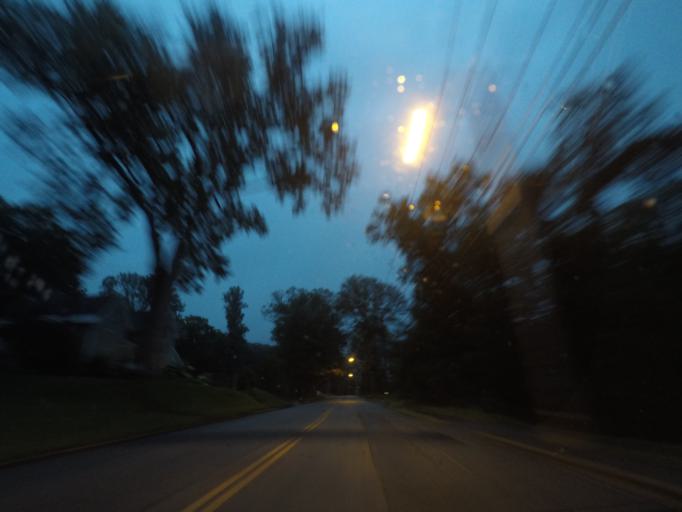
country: US
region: Massachusetts
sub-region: Worcester County
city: Southbridge
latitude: 42.0770
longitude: -72.0557
